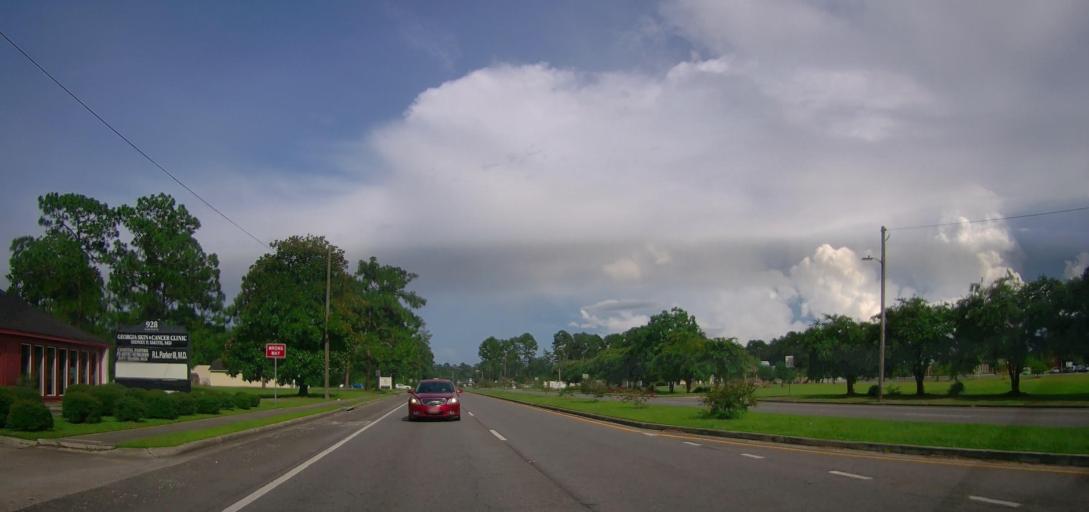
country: US
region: Georgia
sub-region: Wayne County
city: Jesup
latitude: 31.6036
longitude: -81.9002
